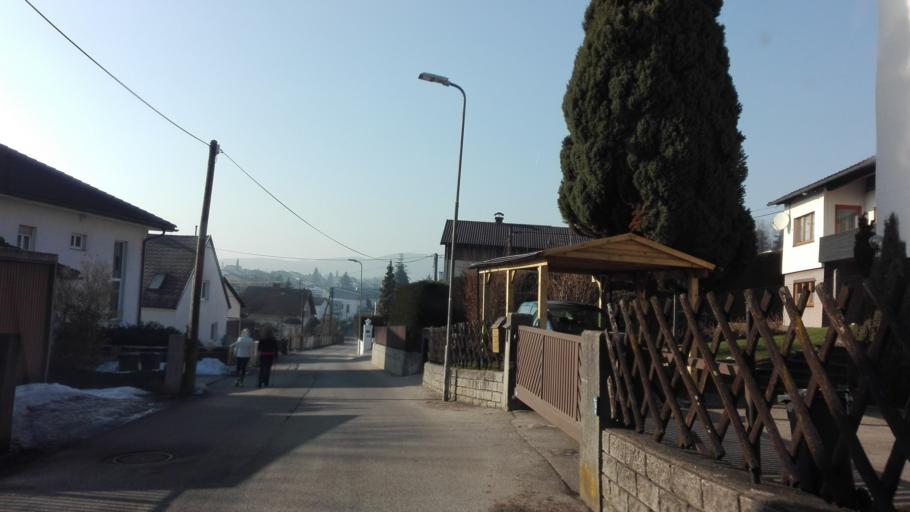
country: AT
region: Upper Austria
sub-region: Politischer Bezirk Linz-Land
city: Leonding
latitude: 48.2813
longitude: 14.2655
